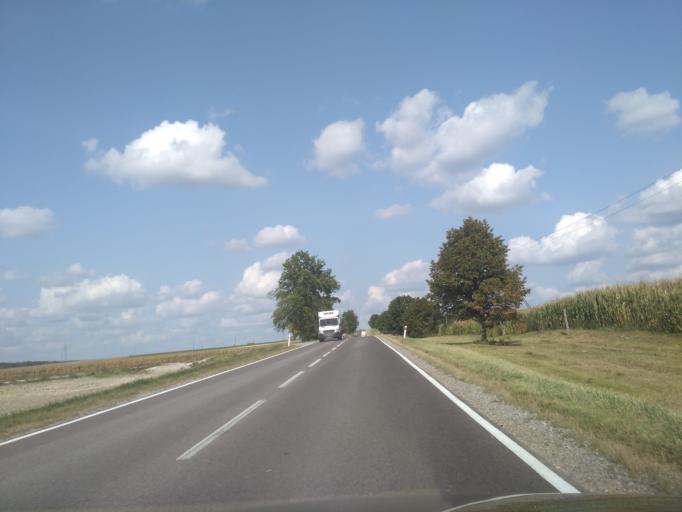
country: PL
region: Lublin Voivodeship
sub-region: Powiat chelmski
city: Rejowiec
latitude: 51.1034
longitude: 23.3064
